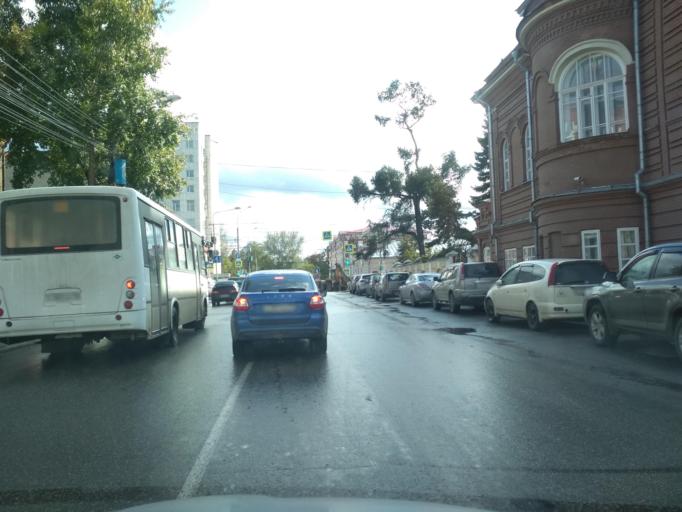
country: RU
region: Tomsk
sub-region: Tomskiy Rayon
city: Tomsk
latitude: 56.4769
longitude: 84.9516
